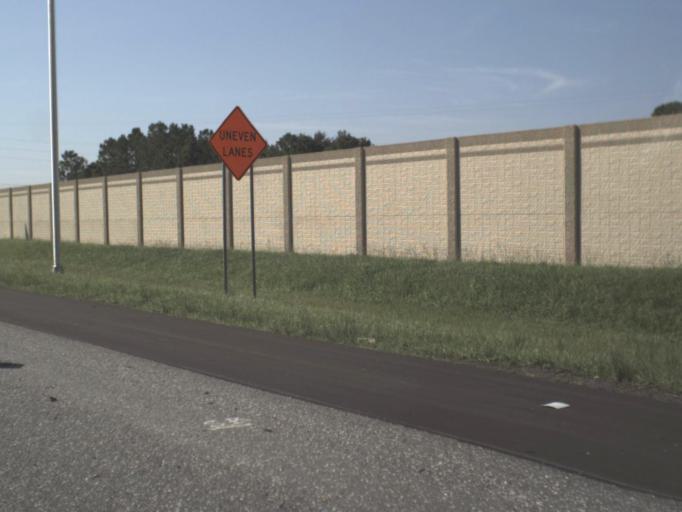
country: US
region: Florida
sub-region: Hillsborough County
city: Pebble Creek
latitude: 28.0949
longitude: -82.3590
